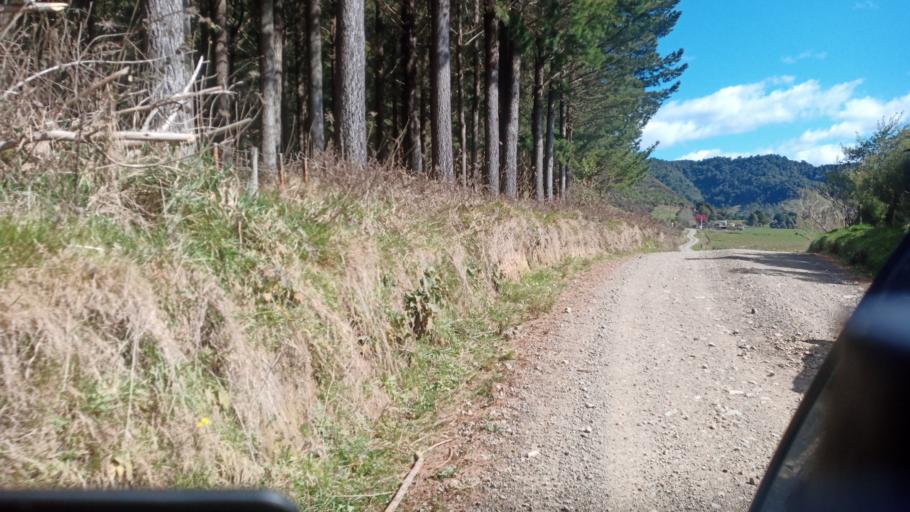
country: NZ
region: Bay of Plenty
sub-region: Opotiki District
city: Opotiki
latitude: -38.1102
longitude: 177.5228
